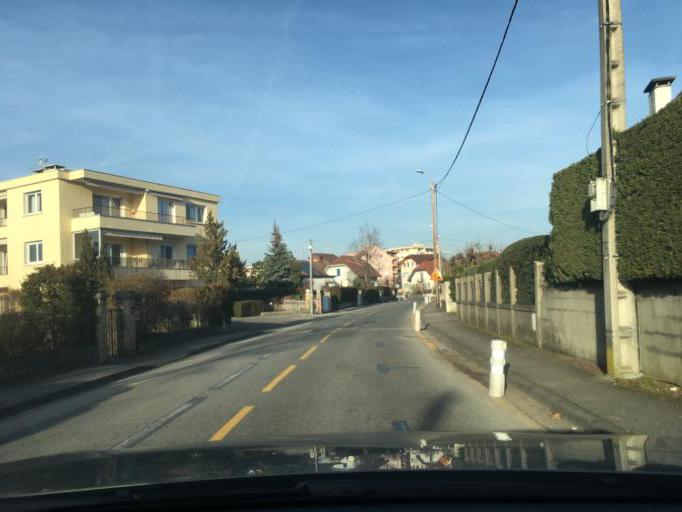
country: FR
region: Rhone-Alpes
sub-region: Departement de la Haute-Savoie
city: Gaillard
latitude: 46.1899
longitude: 6.2172
